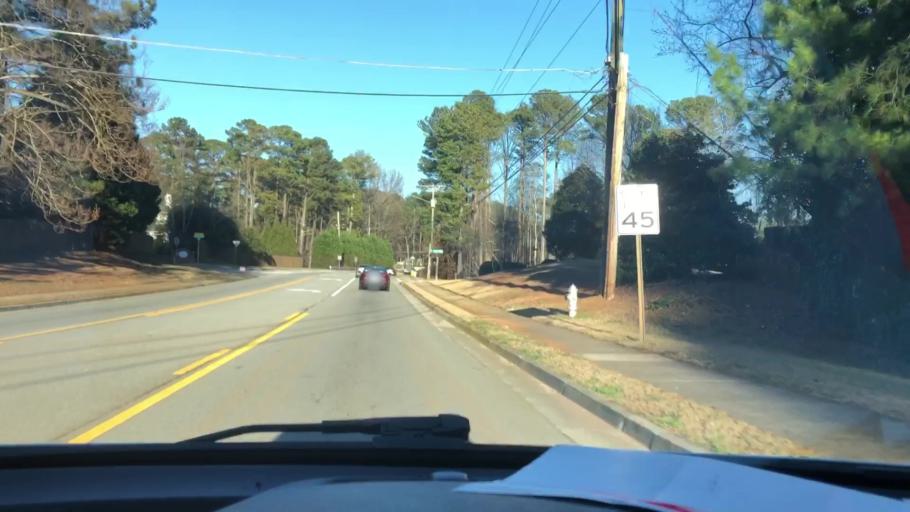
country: US
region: Georgia
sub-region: Gwinnett County
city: Snellville
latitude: 33.9014
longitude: -84.0468
